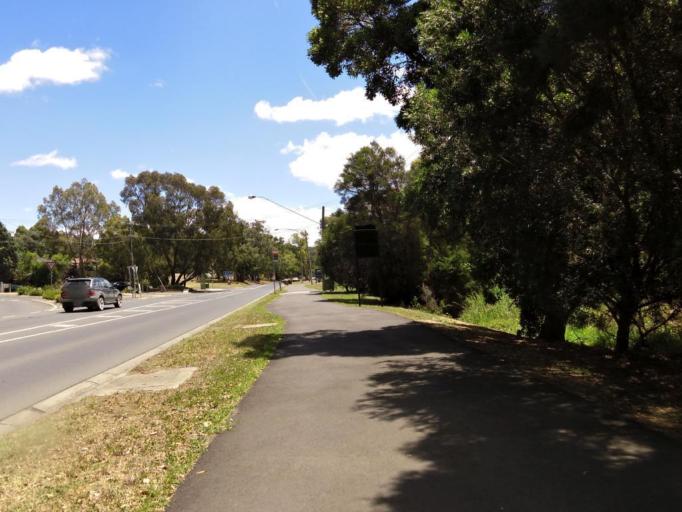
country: AU
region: Victoria
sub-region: Nillumbik
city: Research
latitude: -37.7033
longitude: 145.1769
